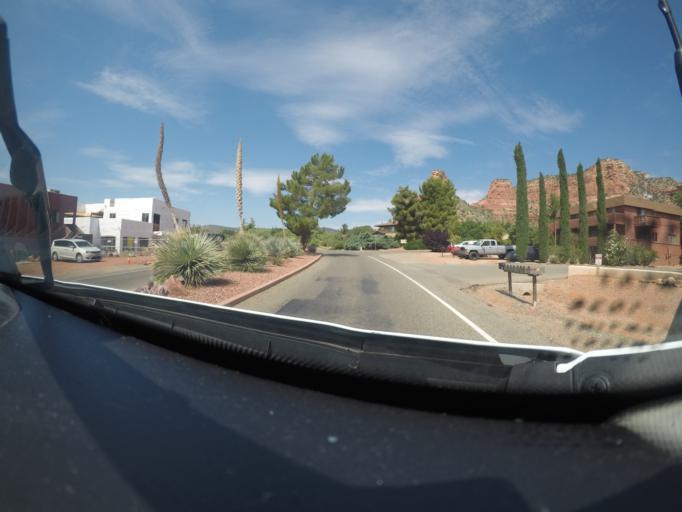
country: US
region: Arizona
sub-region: Yavapai County
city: Village of Oak Creek (Big Park)
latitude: 34.7890
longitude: -111.7645
